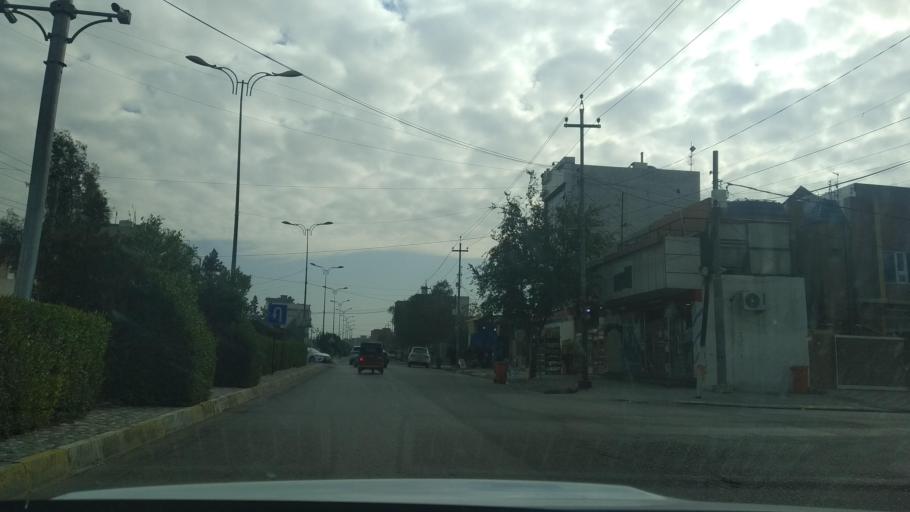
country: IQ
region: Arbil
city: Erbil
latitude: 36.1790
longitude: 44.0273
